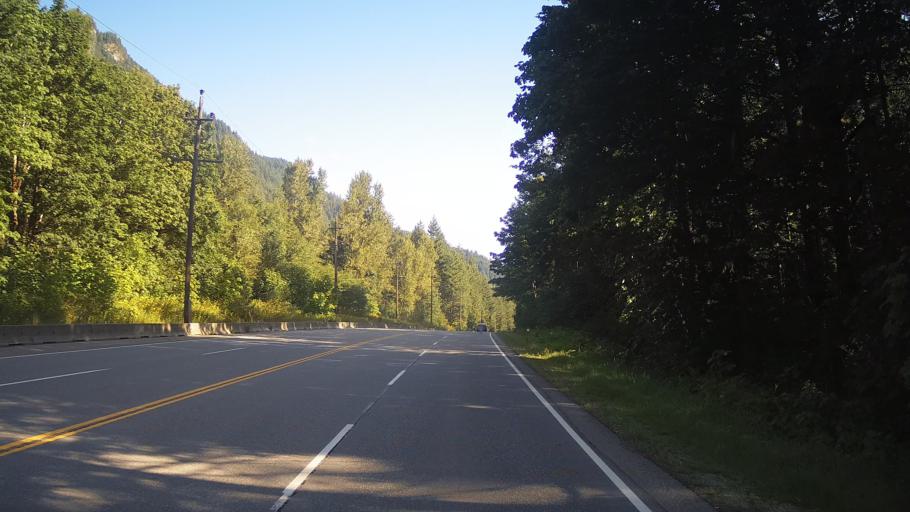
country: CA
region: British Columbia
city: Hope
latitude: 49.4486
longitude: -121.4374
